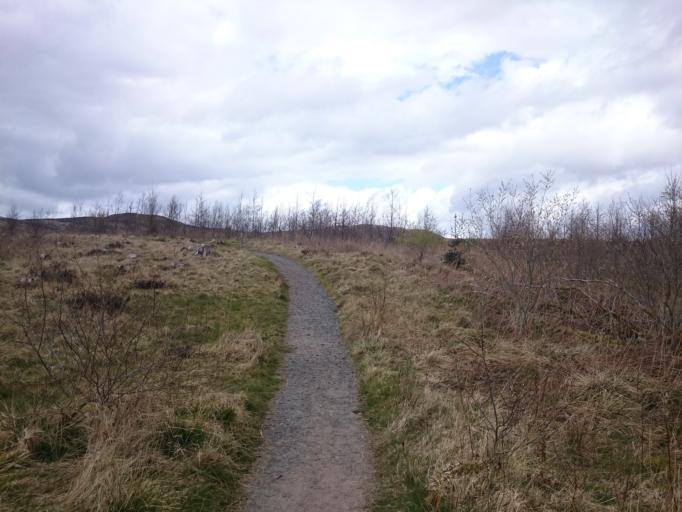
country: GB
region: Scotland
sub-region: Stirling
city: Killearn
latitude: 56.0947
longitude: -4.4888
